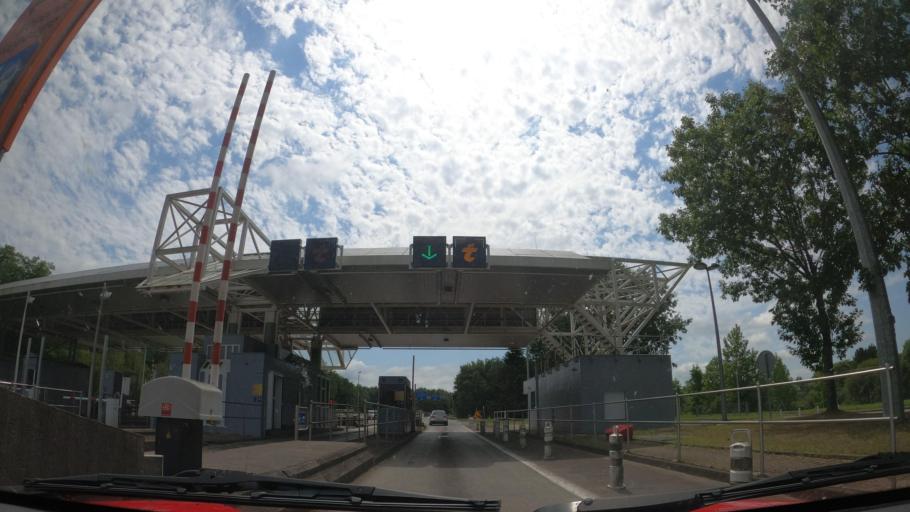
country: FR
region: Aquitaine
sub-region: Departement des Landes
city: Peyrehorade
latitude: 43.5173
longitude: -1.1038
